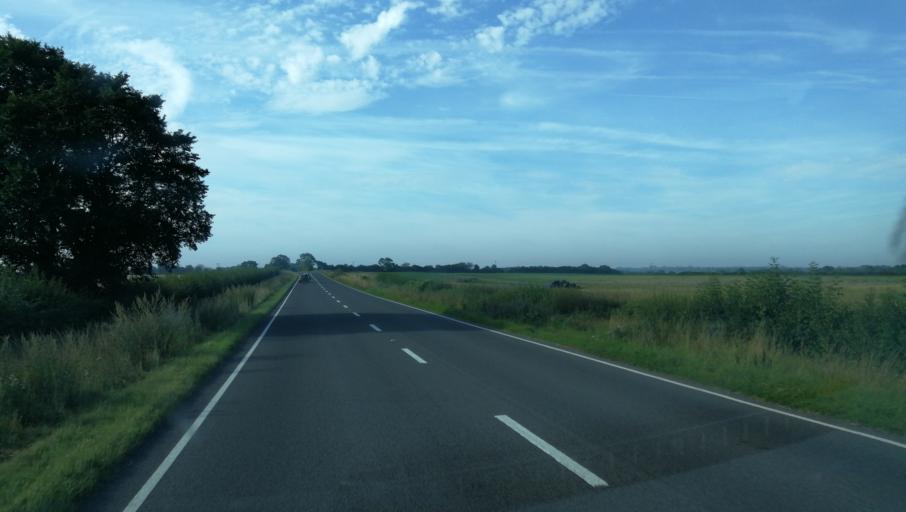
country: GB
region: England
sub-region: Oxfordshire
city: Woodstock
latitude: 51.8811
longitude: -1.3290
